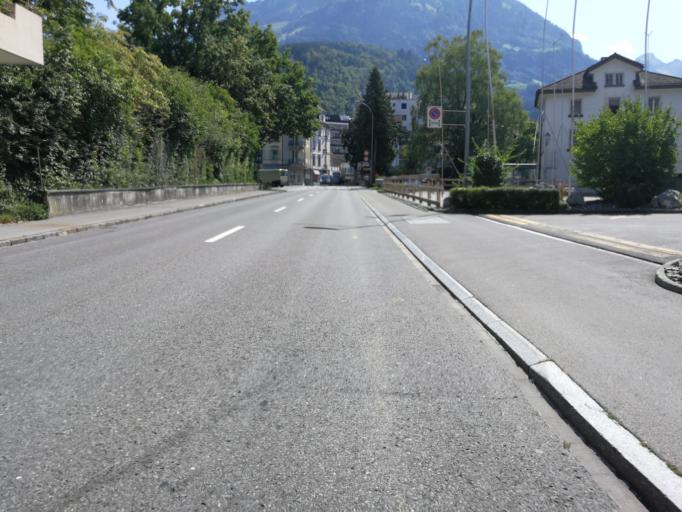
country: CH
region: Schwyz
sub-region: Bezirk Schwyz
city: Ingenbohl
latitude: 46.9950
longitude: 8.6035
